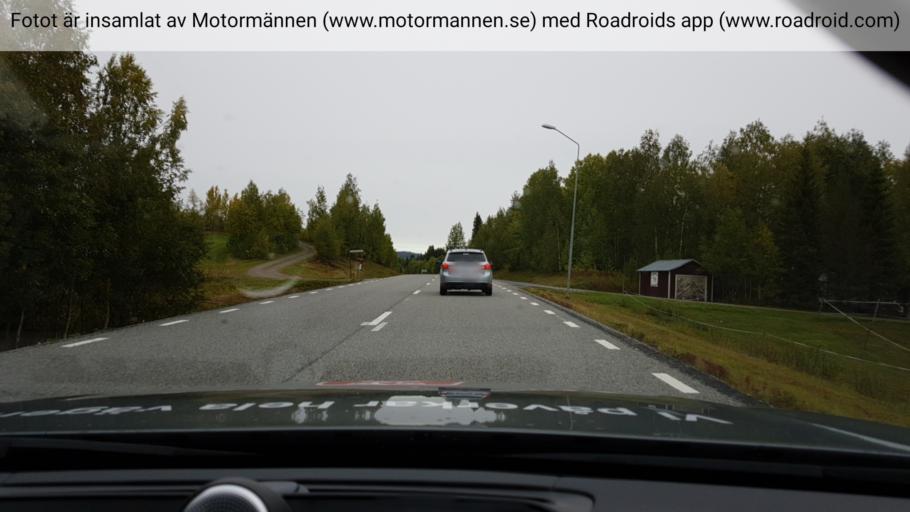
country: SE
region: Jaemtland
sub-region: Stroemsunds Kommun
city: Stroemsund
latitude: 64.0564
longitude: 15.5490
